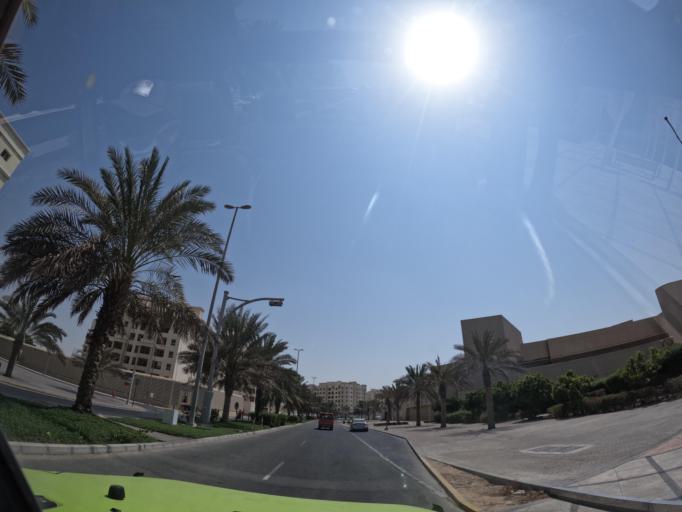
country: AE
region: Abu Dhabi
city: Abu Dhabi
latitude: 24.3135
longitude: 54.6212
